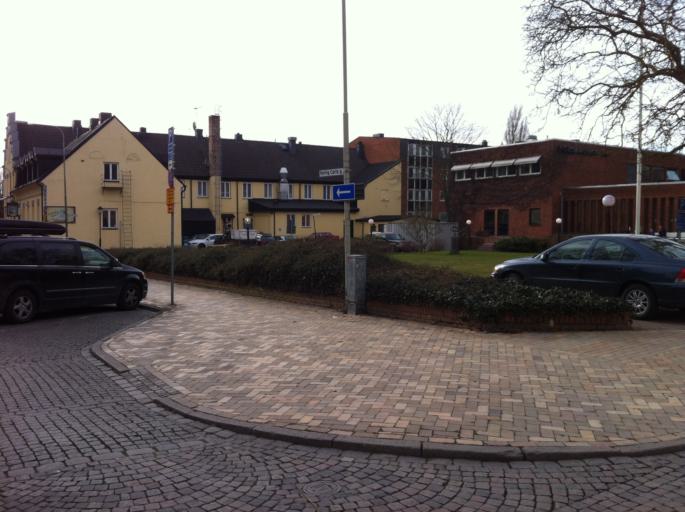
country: SE
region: Skane
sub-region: Kristianstads Kommun
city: Kristianstad
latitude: 56.0325
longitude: 14.1532
